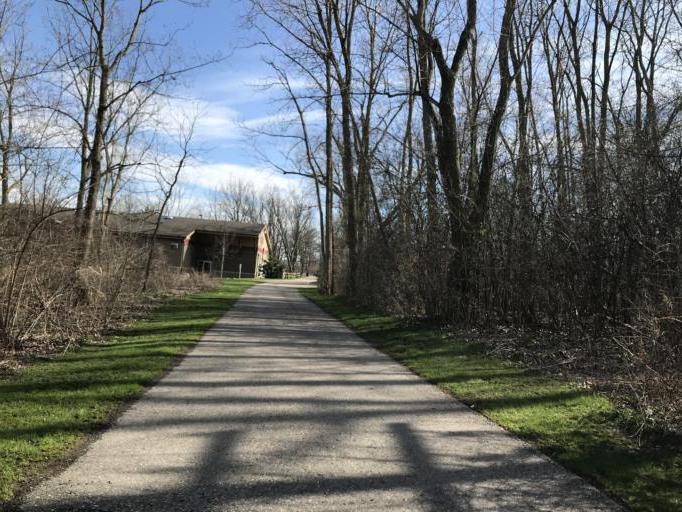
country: US
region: Michigan
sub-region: Washtenaw County
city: Ann Arbor
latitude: 42.2567
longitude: -83.7025
